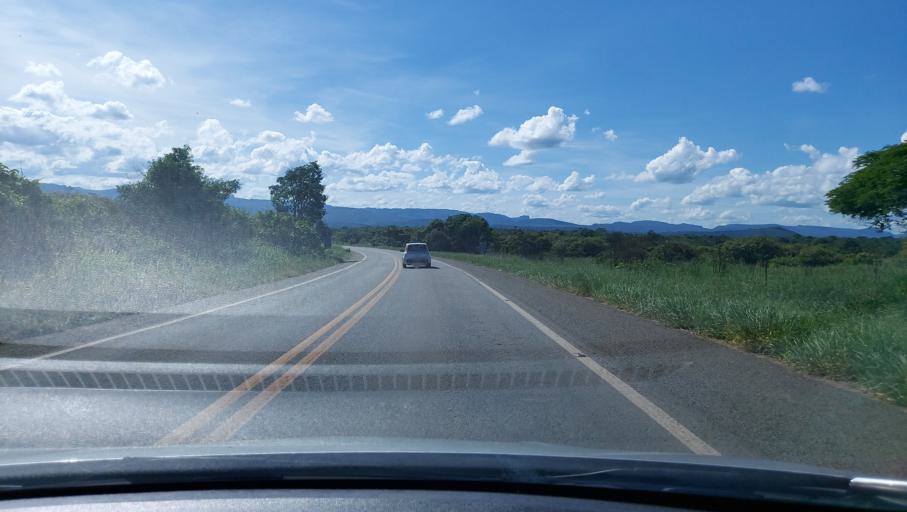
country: BR
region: Bahia
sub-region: Andarai
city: Vera Cruz
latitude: -12.4947
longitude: -41.3023
